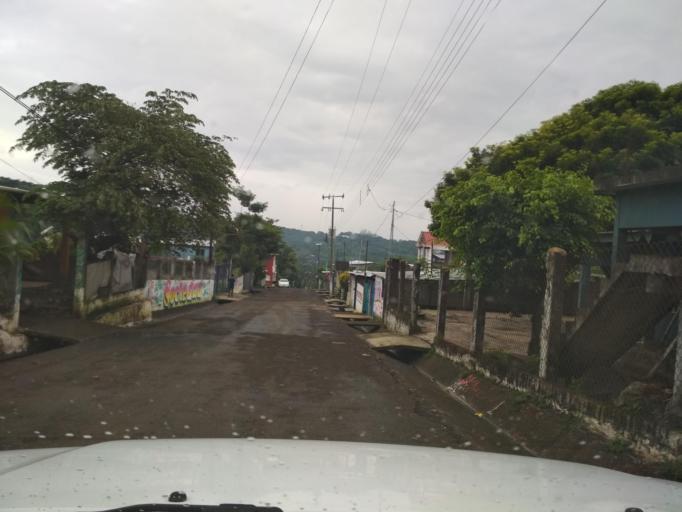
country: MX
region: Veracruz
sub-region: San Andres Tuxtla
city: San Isidro Xoteapan (San Isidro Texcaltitan)
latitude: 18.4618
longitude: -95.2342
